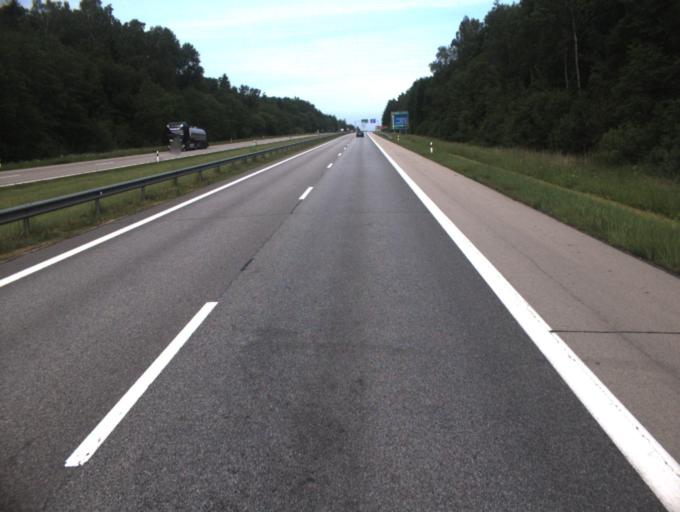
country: LT
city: Raseiniai
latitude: 55.3338
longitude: 23.1138
